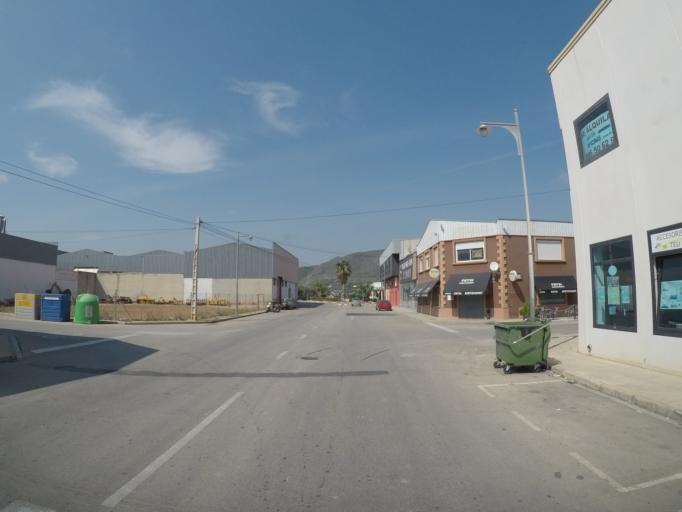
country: ES
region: Valencia
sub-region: Provincia de Alicante
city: Pego
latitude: 38.8475
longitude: -0.1134
